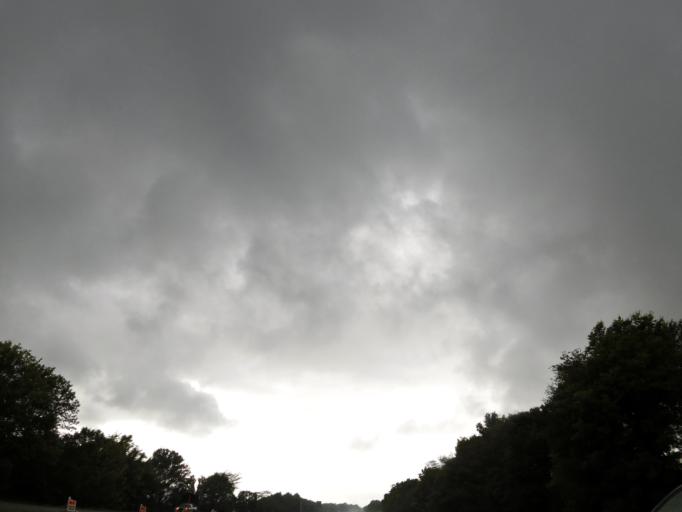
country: US
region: Illinois
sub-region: Jefferson County
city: Mount Vernon
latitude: 38.3435
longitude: -88.9714
